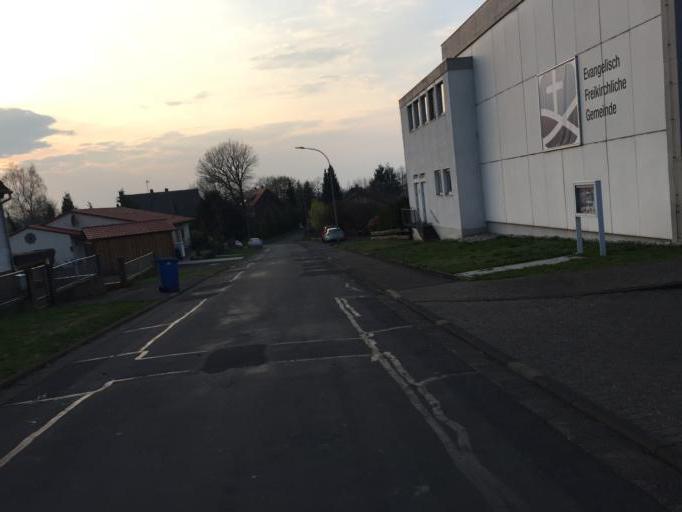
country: DE
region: Hesse
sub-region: Regierungsbezirk Giessen
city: Laubach
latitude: 50.5376
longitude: 8.9958
